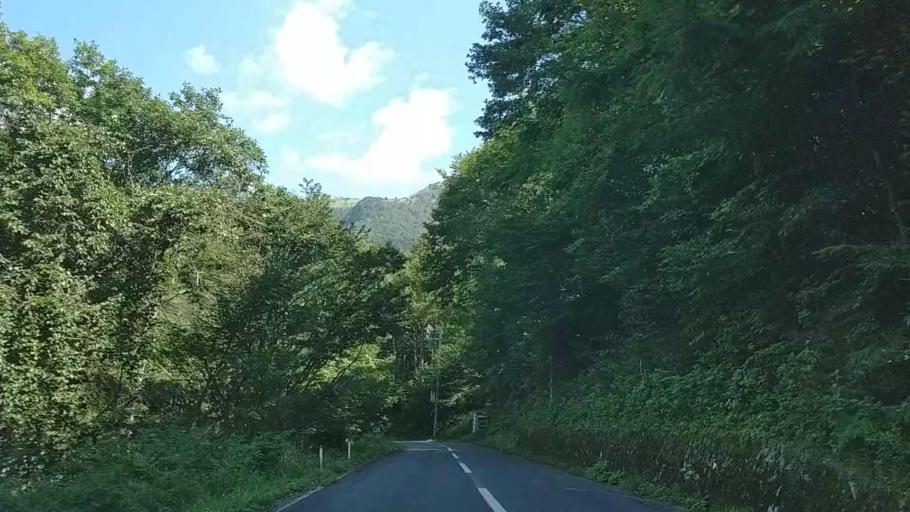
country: JP
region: Nagano
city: Matsumoto
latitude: 36.2044
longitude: 138.1051
